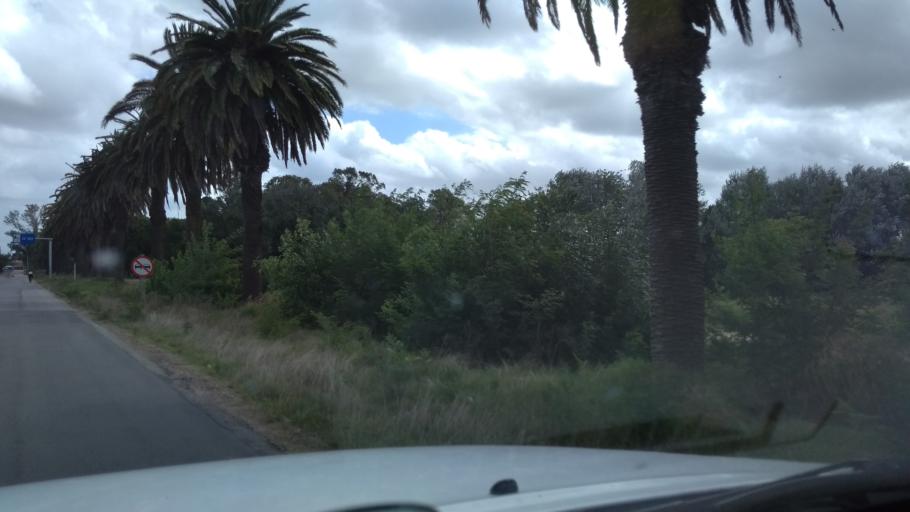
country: UY
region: Canelones
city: San Ramon
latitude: -34.2782
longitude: -55.9527
